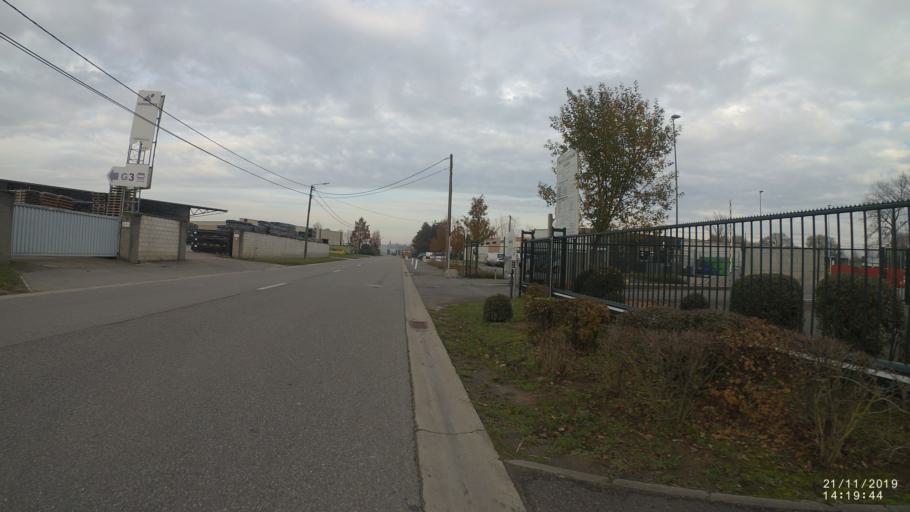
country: BE
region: Flanders
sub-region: Provincie Limburg
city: Alken
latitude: 50.8868
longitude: 5.3014
